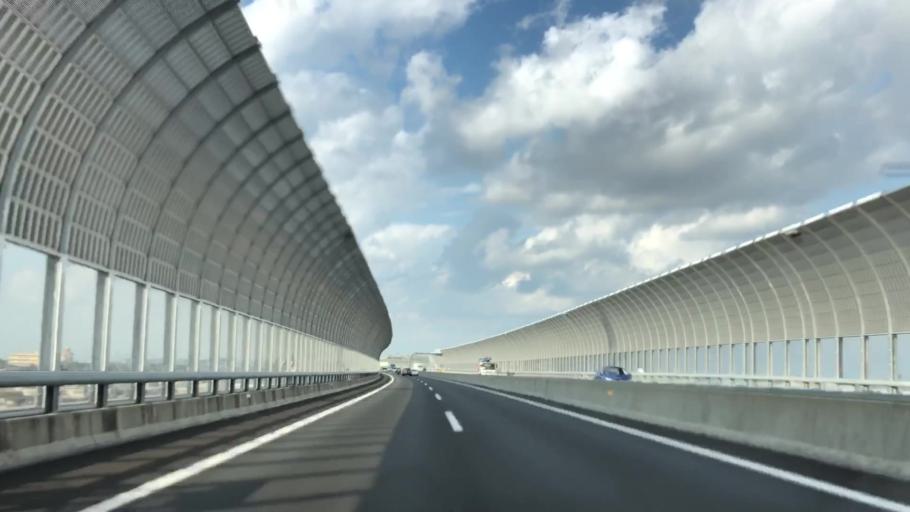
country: JP
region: Chiba
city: Matsudo
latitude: 35.8007
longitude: 139.8780
